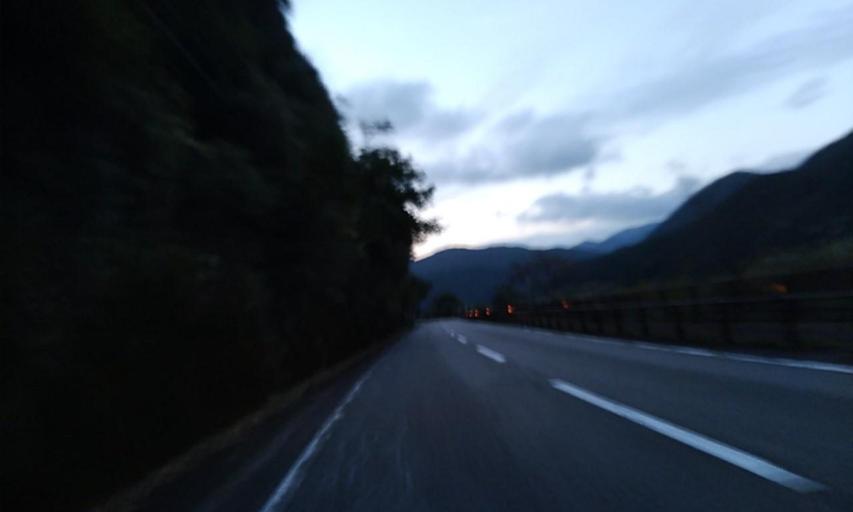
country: JP
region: Wakayama
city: Shingu
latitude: 33.7276
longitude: 135.9511
